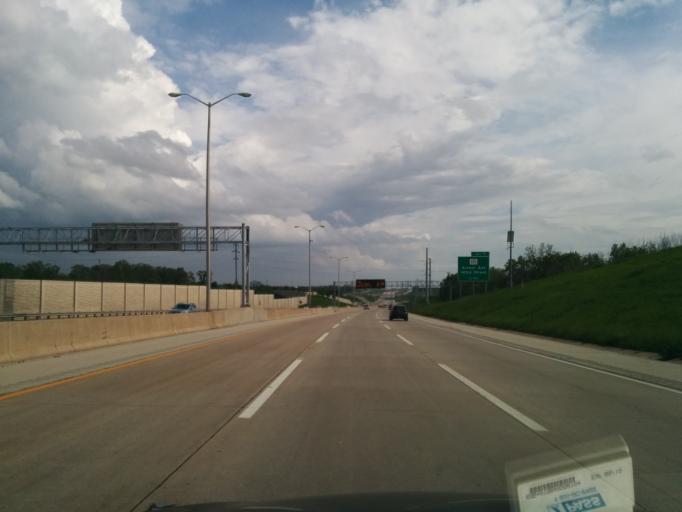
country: US
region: Illinois
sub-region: Cook County
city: Lemont
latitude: 41.6488
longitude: -88.0142
